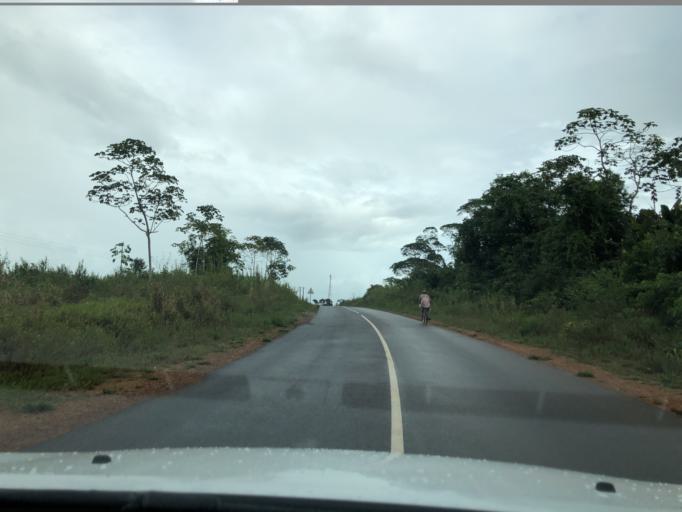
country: GF
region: Guyane
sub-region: Guyane
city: Mana
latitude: 5.5898
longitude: -53.8198
